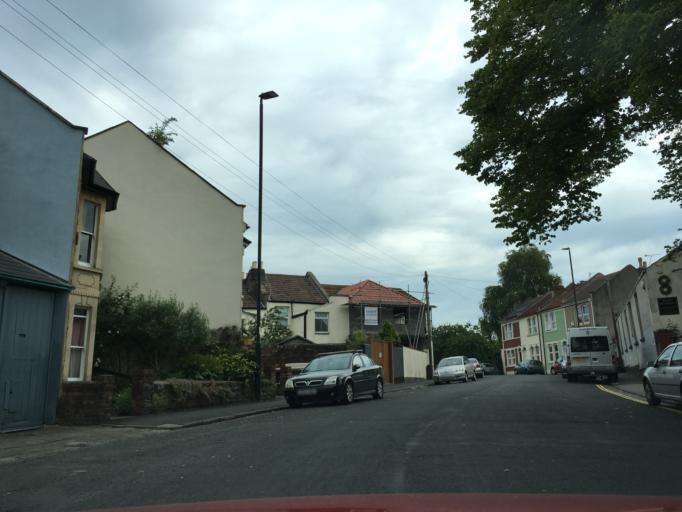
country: GB
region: England
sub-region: Bristol
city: Bristol
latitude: 51.4621
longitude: -2.5580
